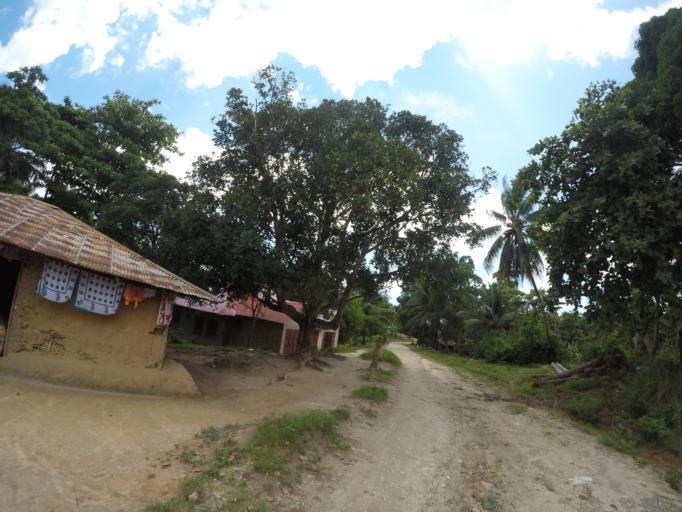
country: TZ
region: Pemba South
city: Mtambile
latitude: -5.3943
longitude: 39.7396
